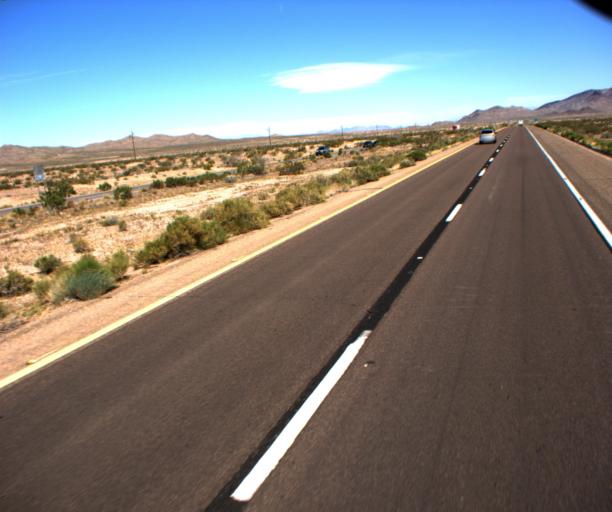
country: US
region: Nevada
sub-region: Clark County
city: Boulder City
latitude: 35.8062
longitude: -114.5400
